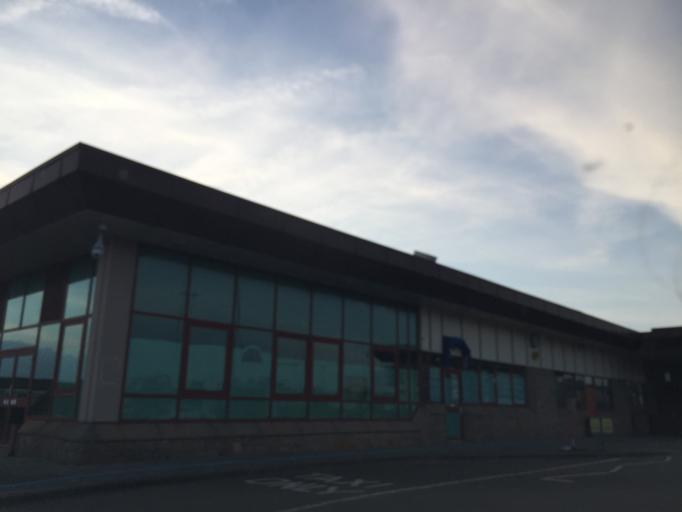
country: JE
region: St Helier
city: Saint Helier
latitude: 49.1792
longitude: -2.1161
